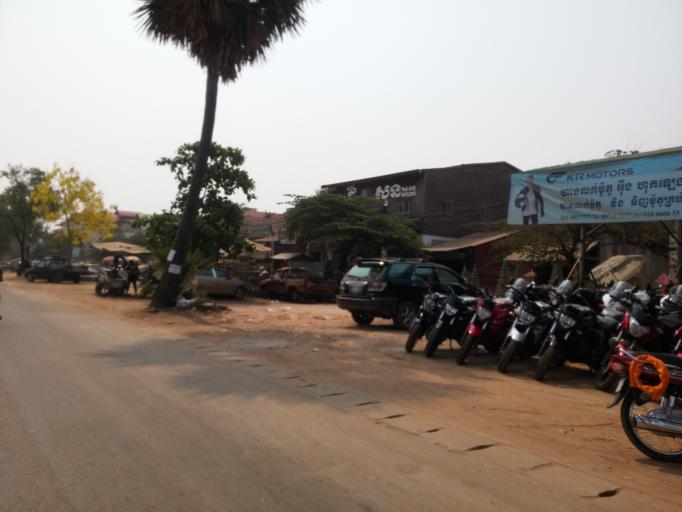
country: KH
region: Siem Reap
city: Siem Reap
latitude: 13.3592
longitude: 103.8825
